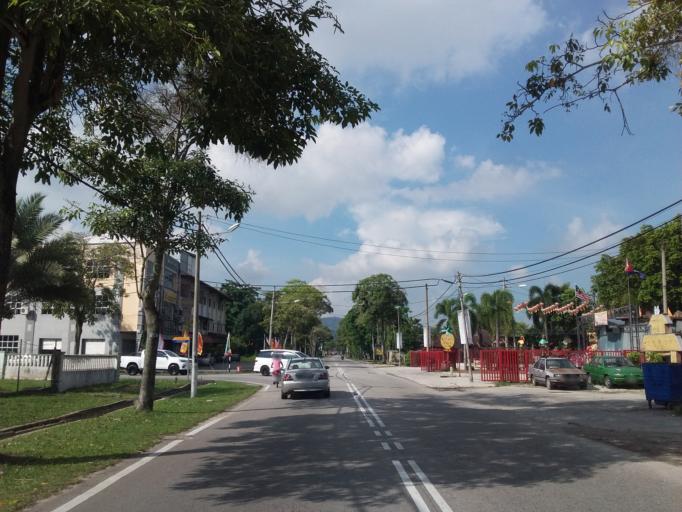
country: MY
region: Johor
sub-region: Daerah Batu Pahat
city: Batu Pahat
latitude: 1.8435
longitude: 102.9245
